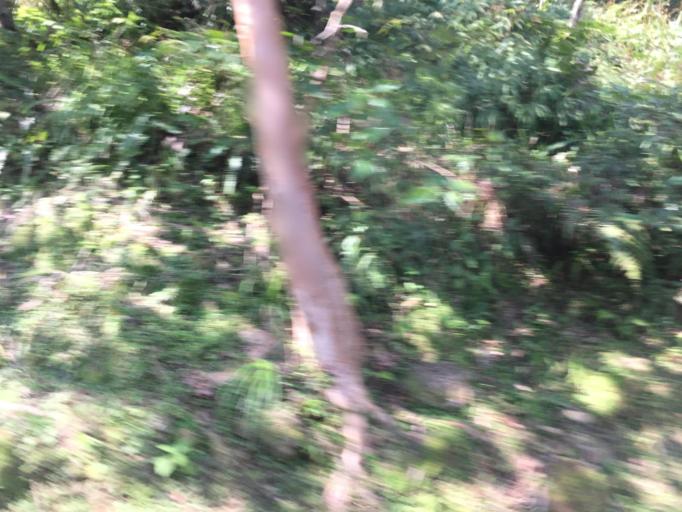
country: TW
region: Taiwan
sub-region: Yilan
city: Yilan
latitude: 24.7568
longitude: 121.5964
